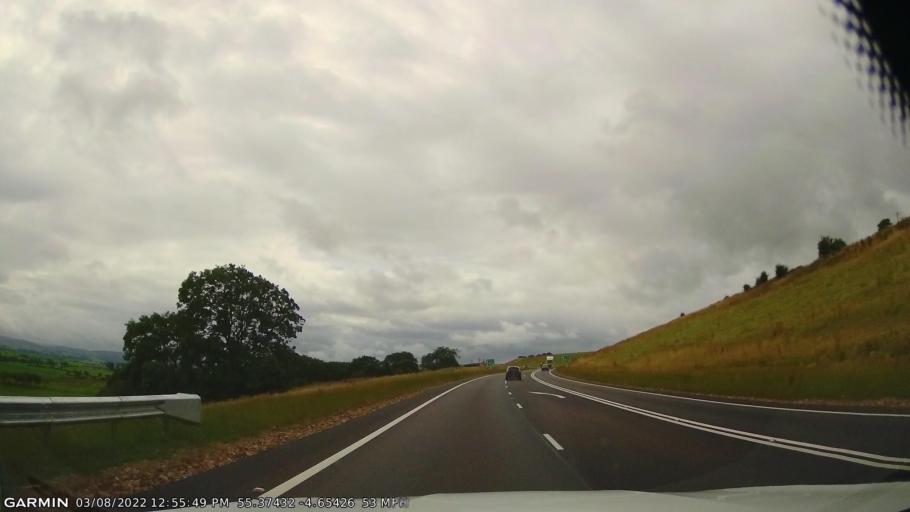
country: GB
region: Scotland
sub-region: South Ayrshire
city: Maybole
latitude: 55.3746
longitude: -4.6542
